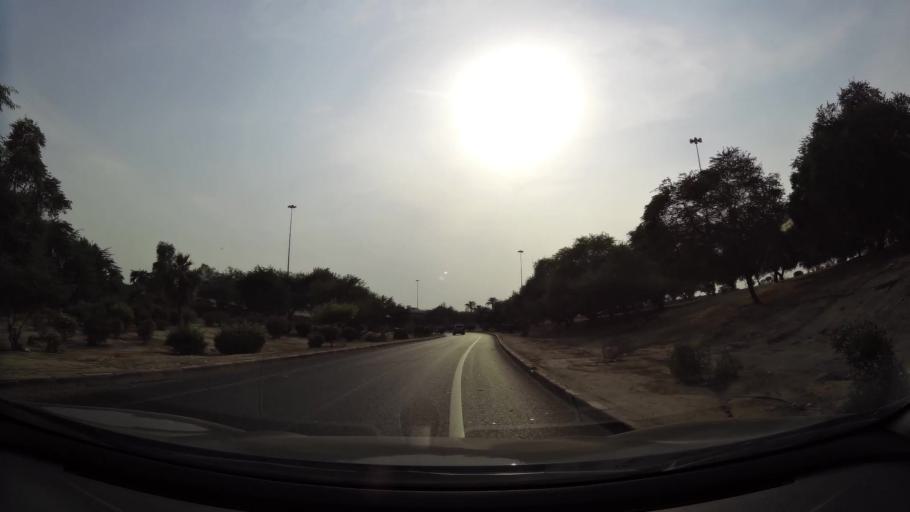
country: KW
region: Al Farwaniyah
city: Janub as Surrah
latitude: 29.2672
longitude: 47.9868
